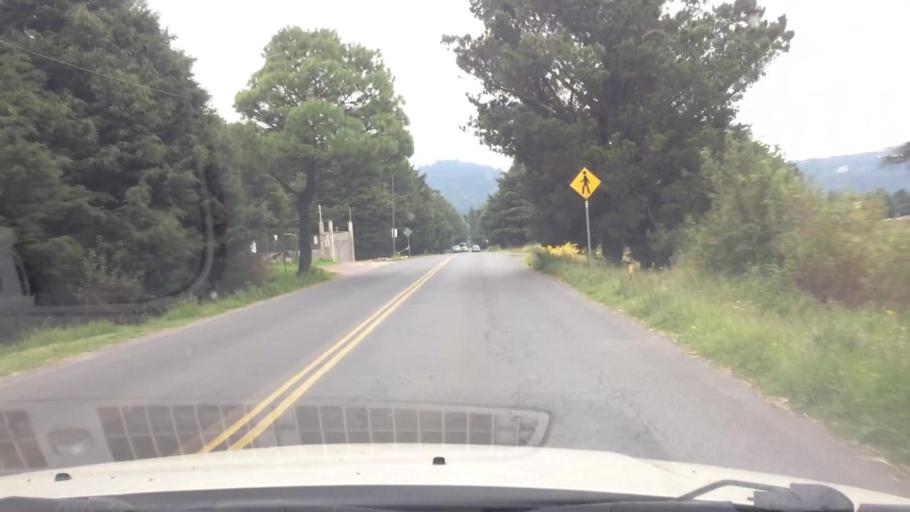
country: MX
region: Mexico City
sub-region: Tlalpan
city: Lomas de Tepemecatl
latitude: 19.2363
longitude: -99.2338
